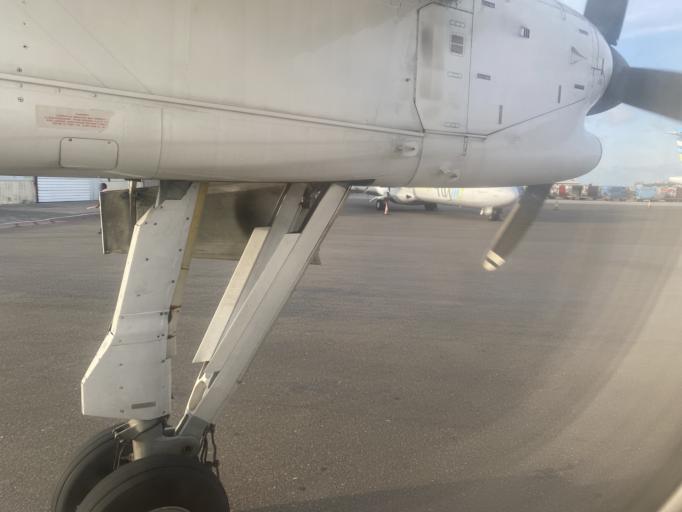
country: MV
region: Maale
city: Male
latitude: 4.1903
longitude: 73.5278
